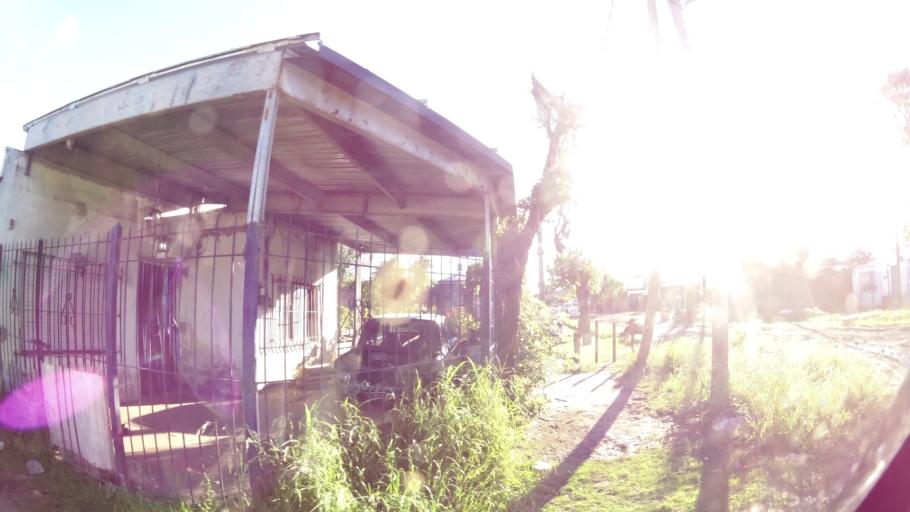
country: AR
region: Buenos Aires
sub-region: Partido de Almirante Brown
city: Adrogue
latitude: -34.7673
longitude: -58.3326
